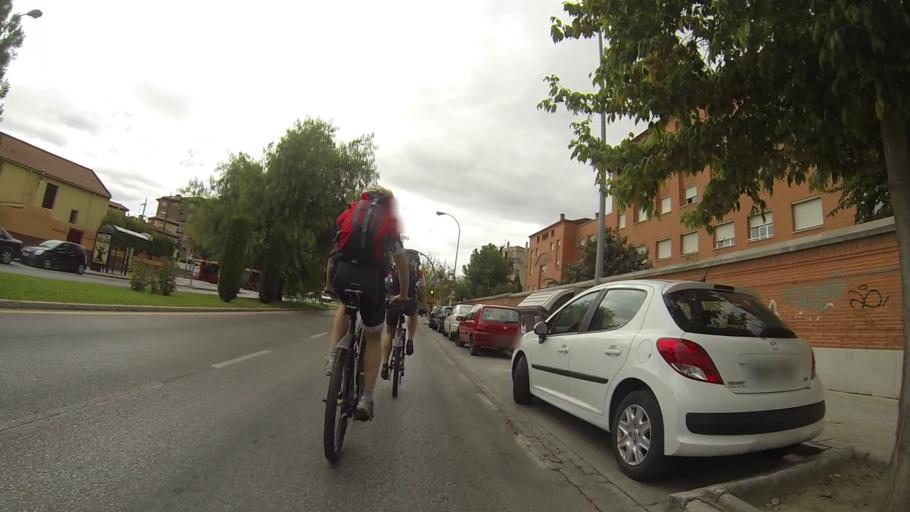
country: ES
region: Andalusia
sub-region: Provincia de Granada
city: Granada
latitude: 37.1917
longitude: -3.6157
